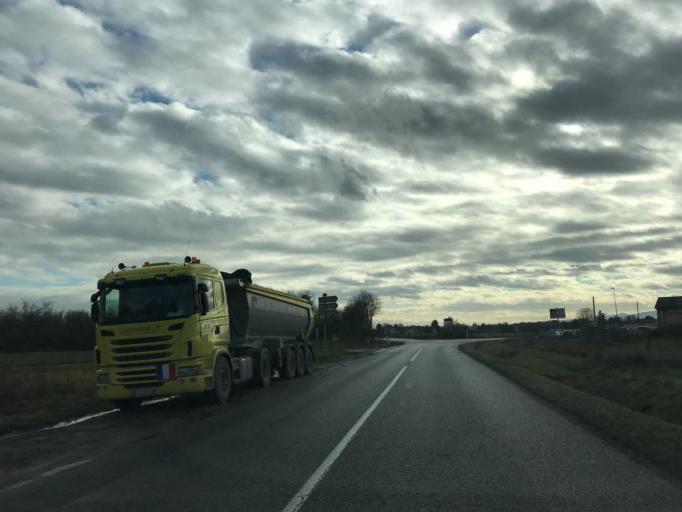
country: FR
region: Rhone-Alpes
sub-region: Departement de l'Ain
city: Sainte-Euphemie
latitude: 45.9582
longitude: 4.8013
